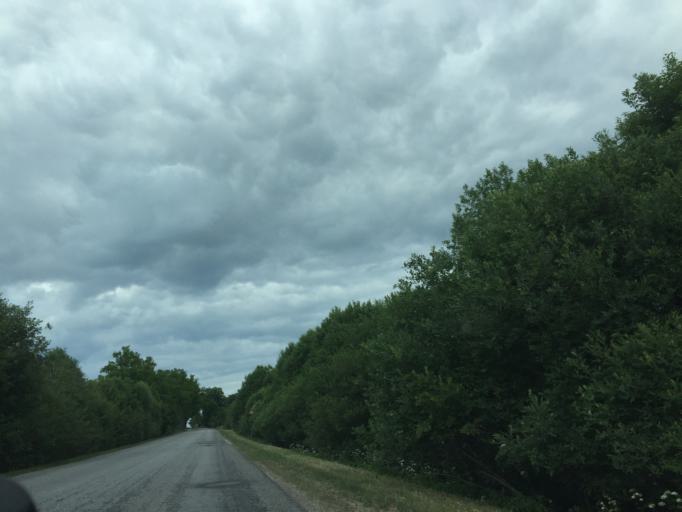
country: LV
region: Skriveri
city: Skriveri
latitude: 56.8310
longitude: 25.1286
